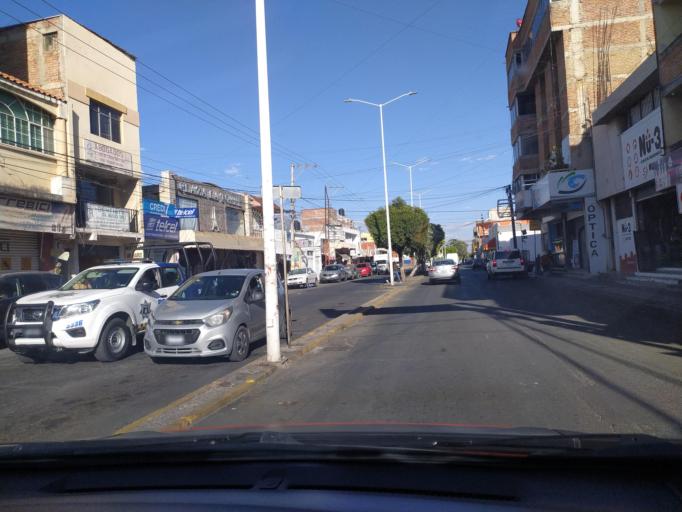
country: LA
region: Oudomxai
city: Muang La
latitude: 21.0155
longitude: 101.8576
